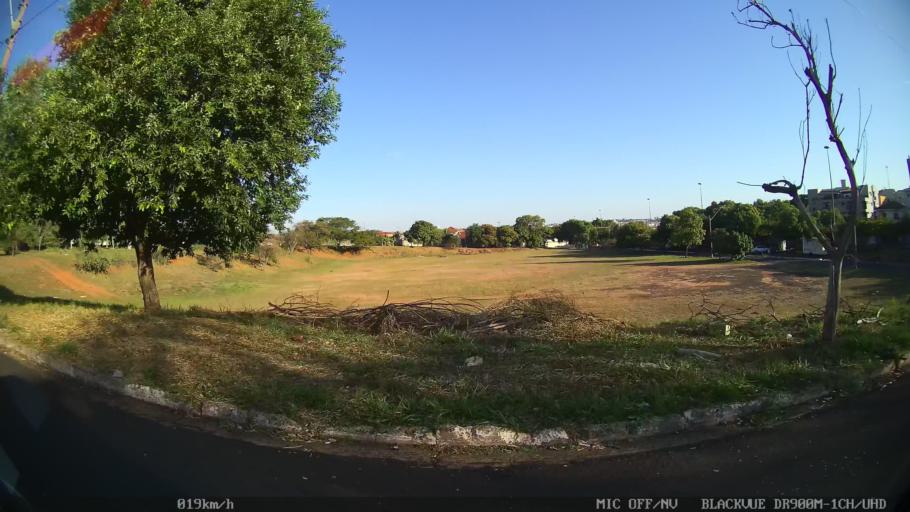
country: BR
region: Sao Paulo
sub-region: Sao Jose Do Rio Preto
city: Sao Jose do Rio Preto
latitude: -20.7989
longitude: -49.3585
